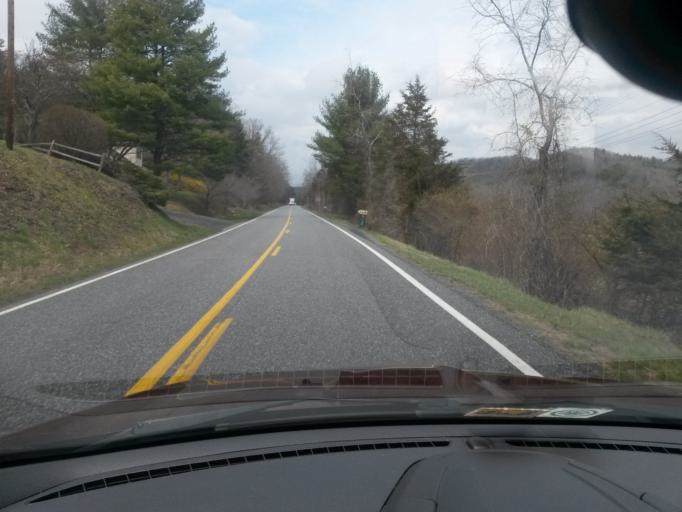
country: US
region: Virginia
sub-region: Bath County
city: Warm Springs
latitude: 38.0301
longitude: -79.6510
